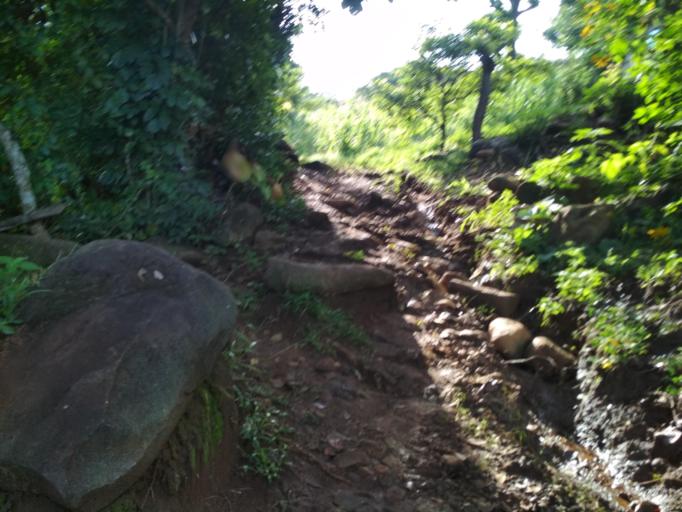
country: MX
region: Veracruz
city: Catemaco
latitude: 18.3885
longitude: -95.1242
